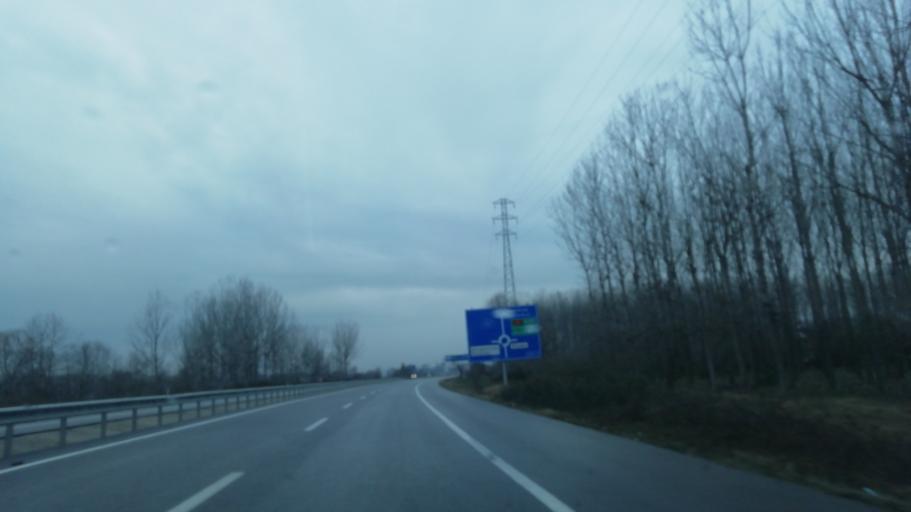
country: TR
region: Sakarya
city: Akyazi
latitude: 40.6555
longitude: 30.5990
